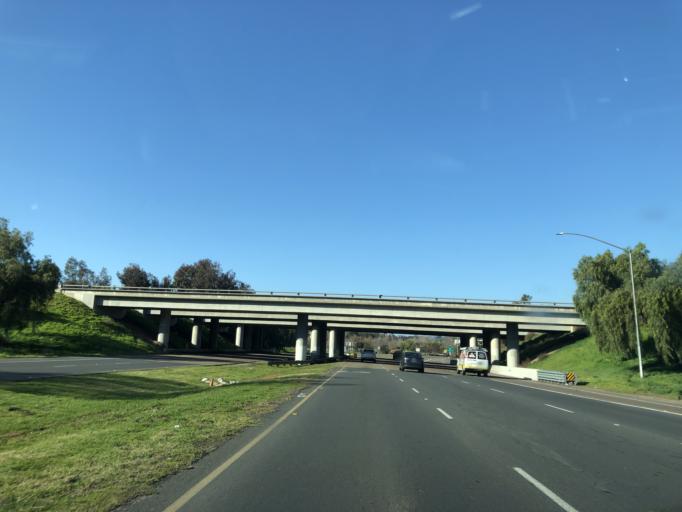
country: US
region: California
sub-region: San Diego County
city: Escondido
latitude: 33.1299
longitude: -117.0923
